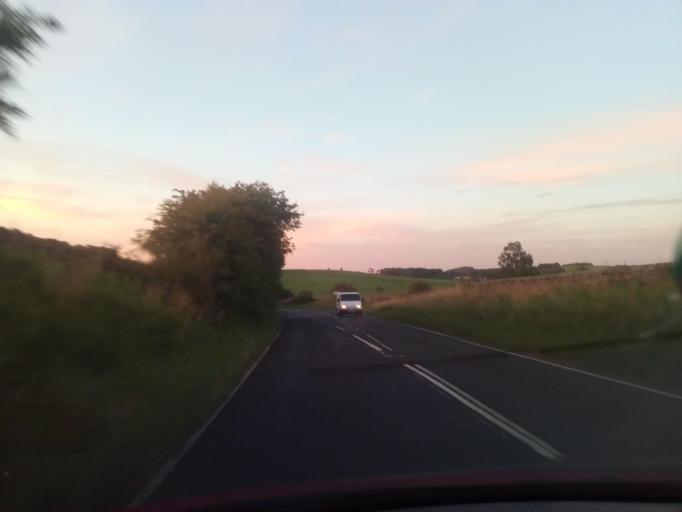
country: GB
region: England
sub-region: Northumberland
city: Bardon Mill
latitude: 54.9379
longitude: -2.2871
